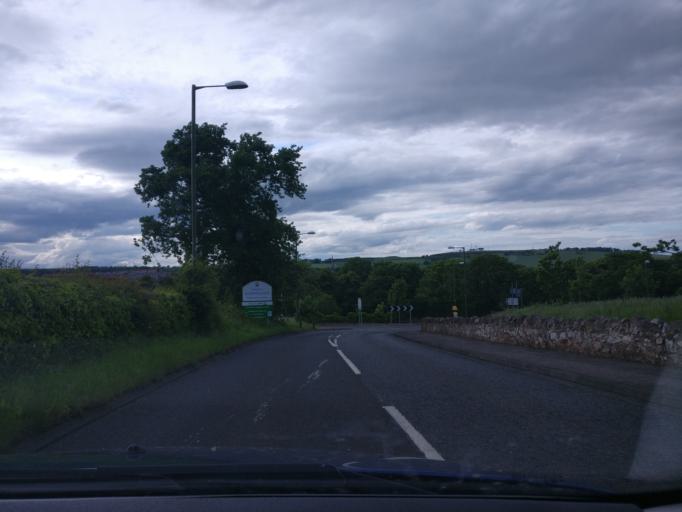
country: GB
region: Scotland
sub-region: East Lothian
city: Haddington
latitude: 55.9496
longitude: -2.7735
